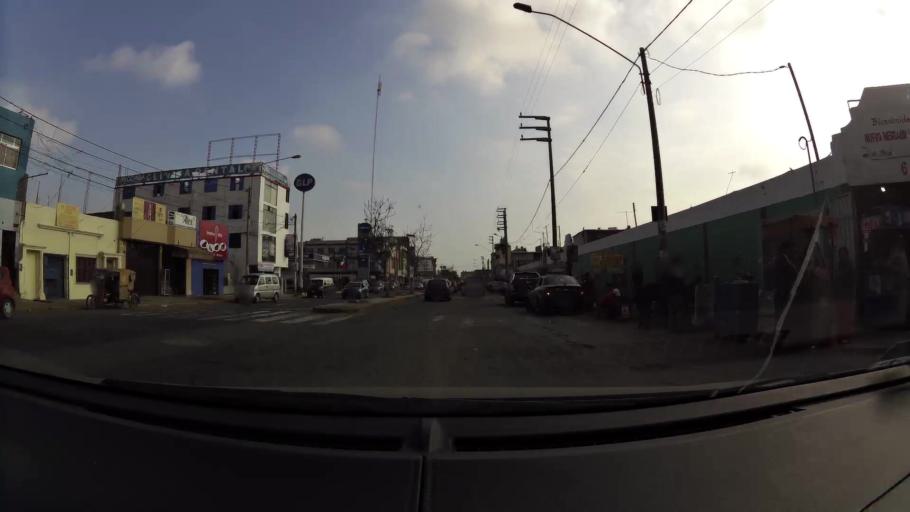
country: PE
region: La Libertad
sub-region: Provincia de Trujillo
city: Trujillo
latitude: -8.1054
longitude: -79.0205
